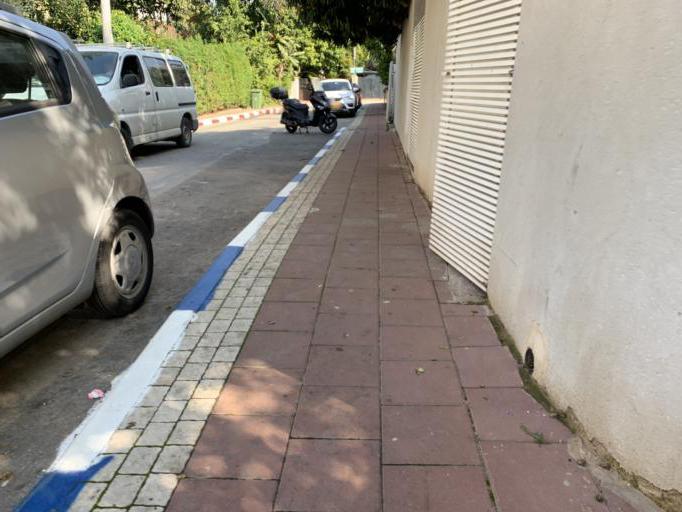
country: IL
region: Tel Aviv
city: Ramat Gan
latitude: 32.0948
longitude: 34.8172
